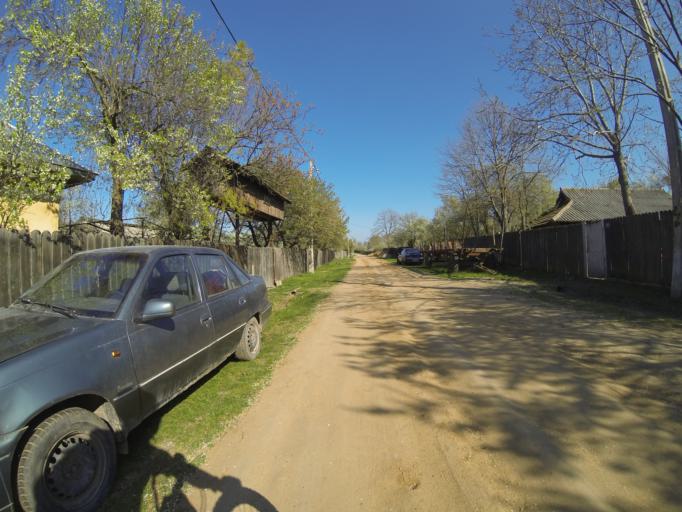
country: RO
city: Varvoru
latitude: 44.2257
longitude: 23.6467
